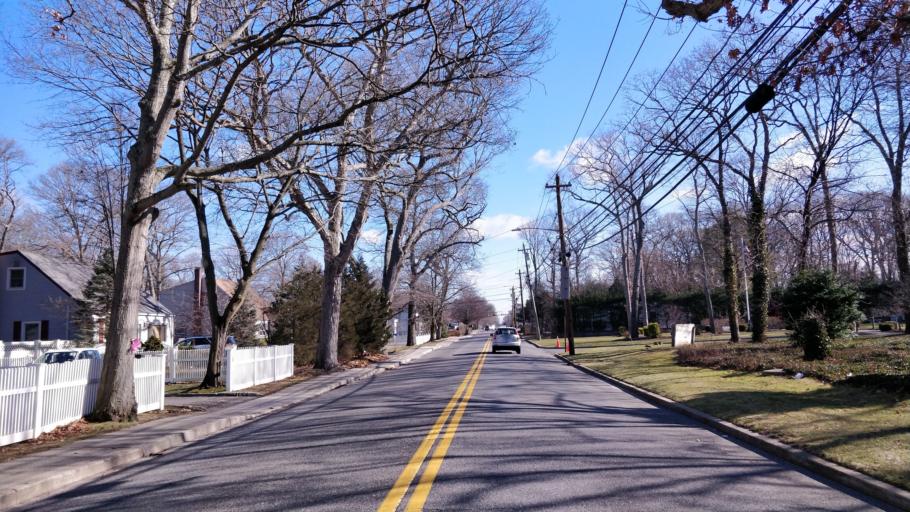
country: US
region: New York
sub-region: Suffolk County
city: Saint James
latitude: 40.8753
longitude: -73.1593
